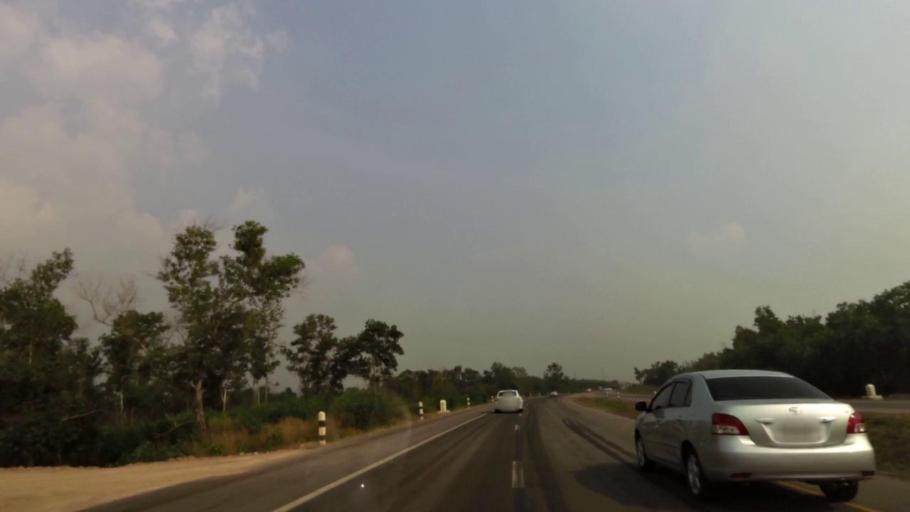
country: TH
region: Rayong
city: Klaeng
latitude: 12.8082
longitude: 101.6478
